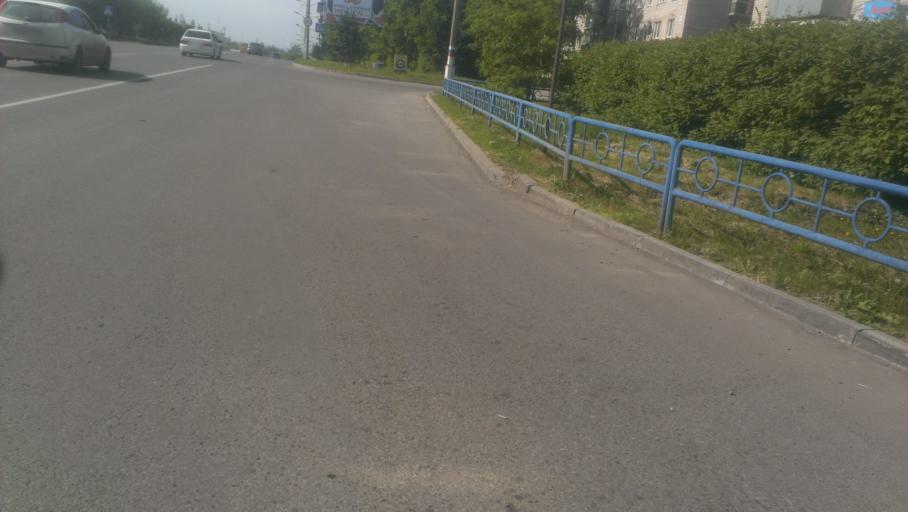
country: RU
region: Altai Krai
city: Novoaltaysk
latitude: 53.3939
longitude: 83.9332
